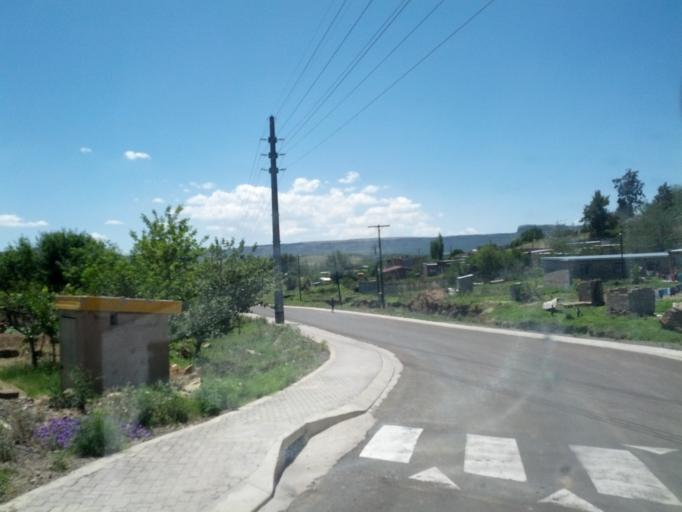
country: LS
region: Maseru
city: Maseru
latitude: -29.3060
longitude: 27.4898
